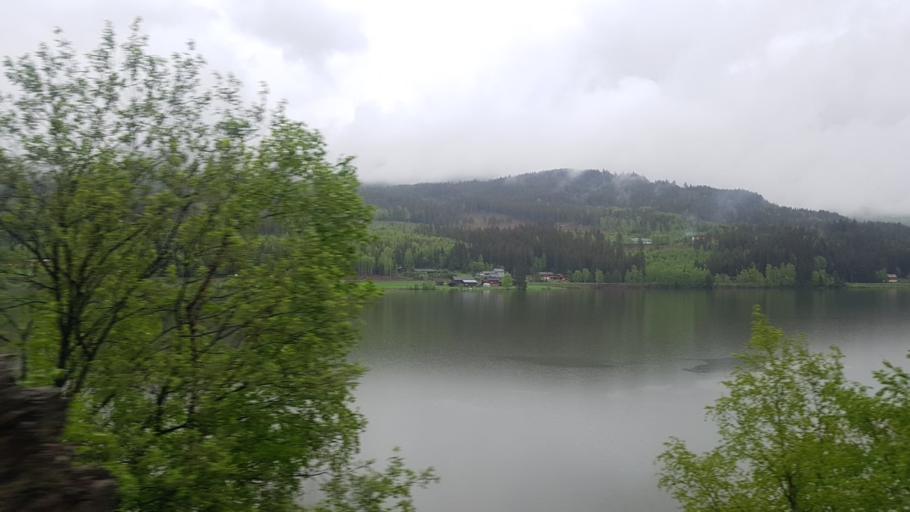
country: NO
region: Oppland
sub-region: Oyer
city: Tretten
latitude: 61.3087
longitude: 10.2919
